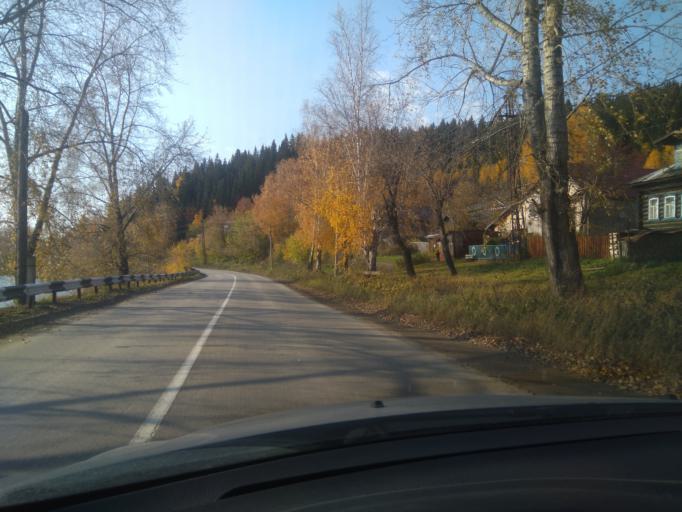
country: RU
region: Sverdlovsk
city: Nizhniye Sergi
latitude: 56.6744
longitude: 59.3204
